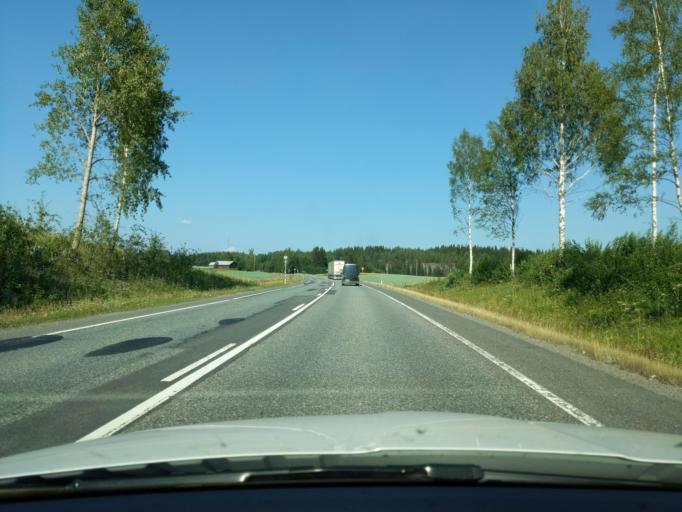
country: FI
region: Paijanne Tavastia
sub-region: Lahti
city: Hollola
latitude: 60.9658
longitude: 25.4617
